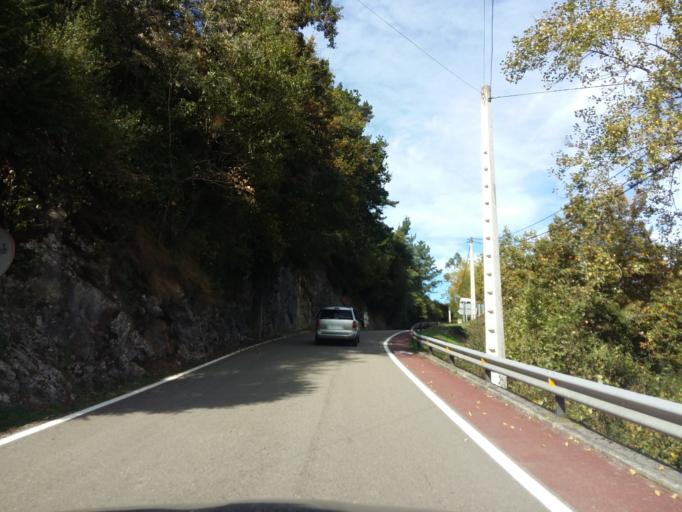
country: ES
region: Cantabria
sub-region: Provincia de Cantabria
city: San Vicente de la Barquera
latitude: 43.3077
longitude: -4.4714
